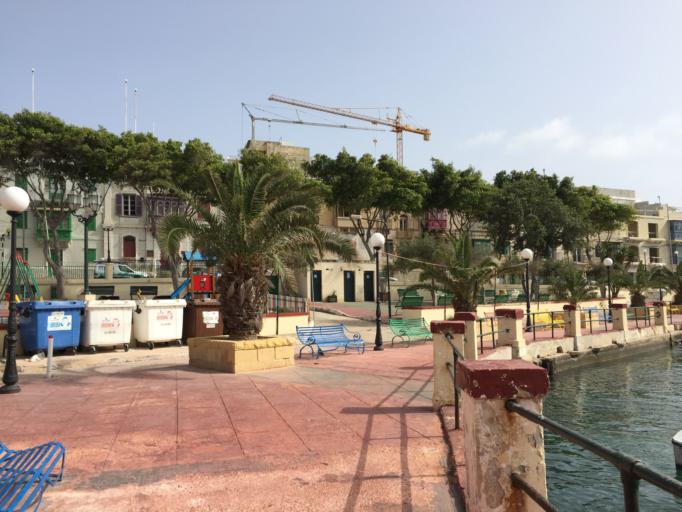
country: MT
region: Bormla
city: Cospicua
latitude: 35.8888
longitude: 14.5273
